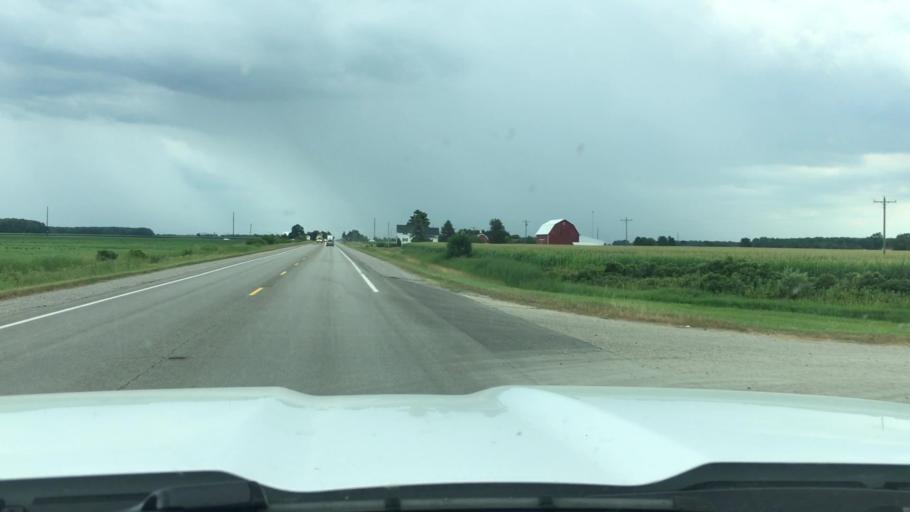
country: US
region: Michigan
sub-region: Montcalm County
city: Carson City
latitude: 43.1764
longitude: -84.7880
